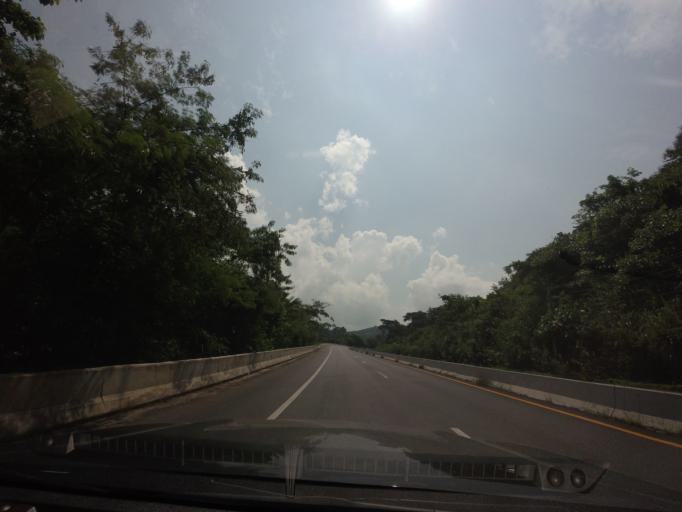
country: TH
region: Phrae
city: Den Chai
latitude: 17.8754
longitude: 100.0453
